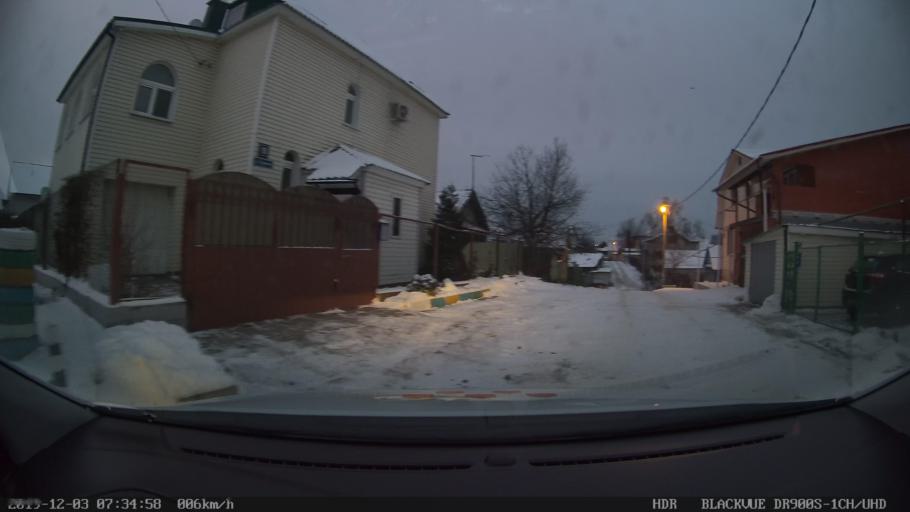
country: RU
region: Tatarstan
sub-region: Gorod Kazan'
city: Kazan
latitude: 55.7504
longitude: 49.1753
